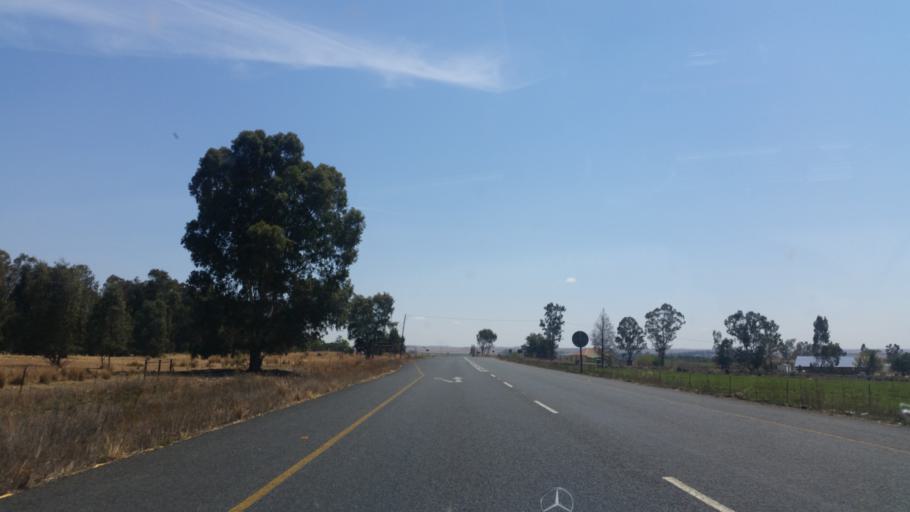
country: ZA
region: Orange Free State
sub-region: Thabo Mofutsanyana District Municipality
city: Phuthaditjhaba
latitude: -28.2127
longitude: 28.6938
